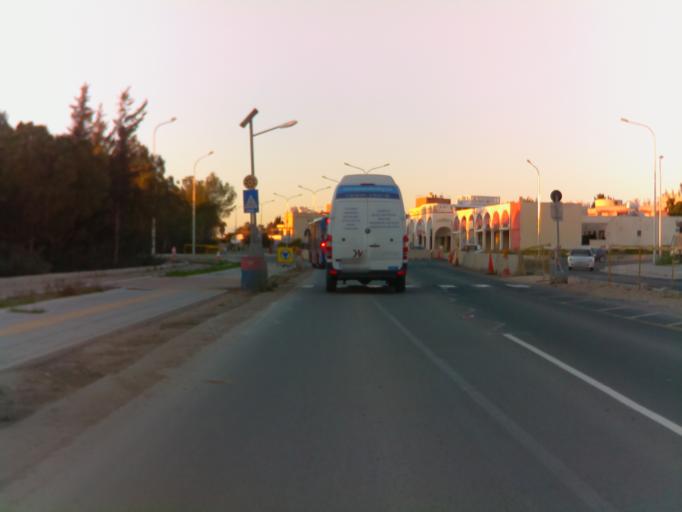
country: CY
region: Pafos
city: Paphos
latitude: 34.7743
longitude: 32.4088
